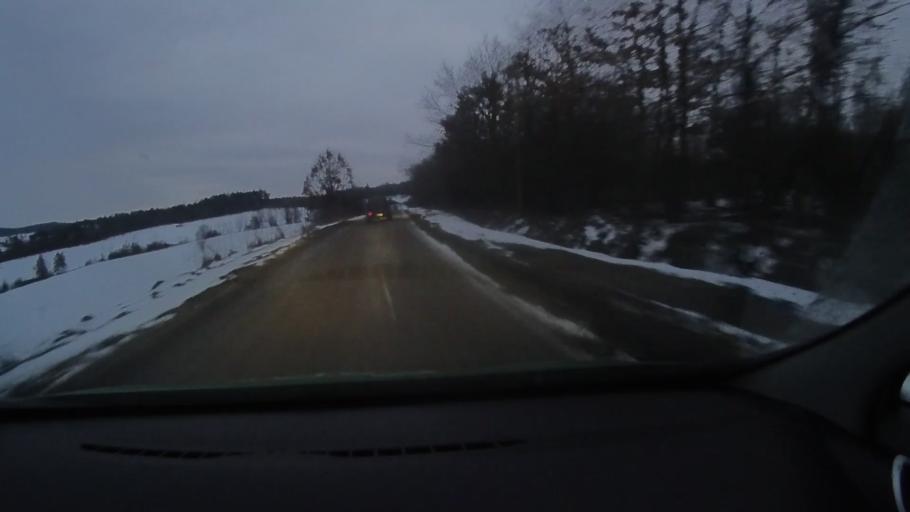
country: RO
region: Harghita
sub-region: Comuna Darjiu
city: Darjiu
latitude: 46.1884
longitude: 25.2474
